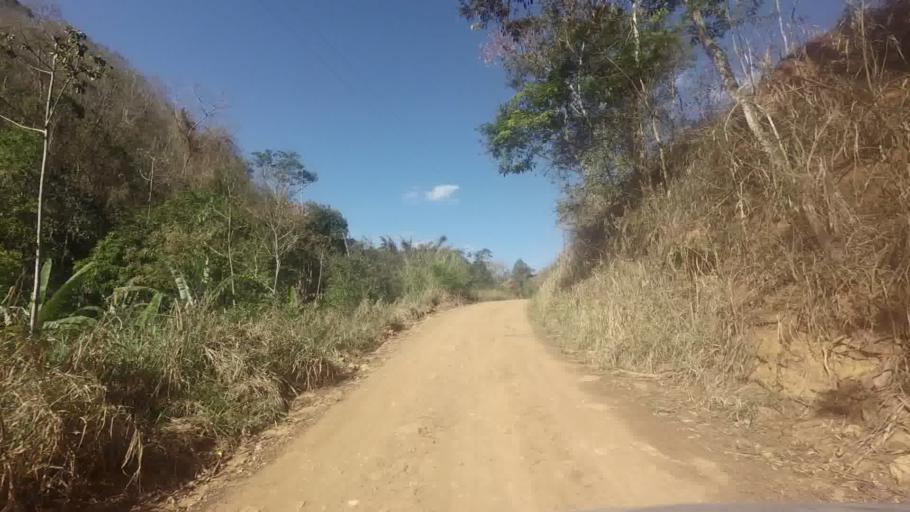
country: BR
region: Espirito Santo
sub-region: Sao Jose Do Calcado
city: Sao Jose do Calcado
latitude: -21.0313
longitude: -41.5918
